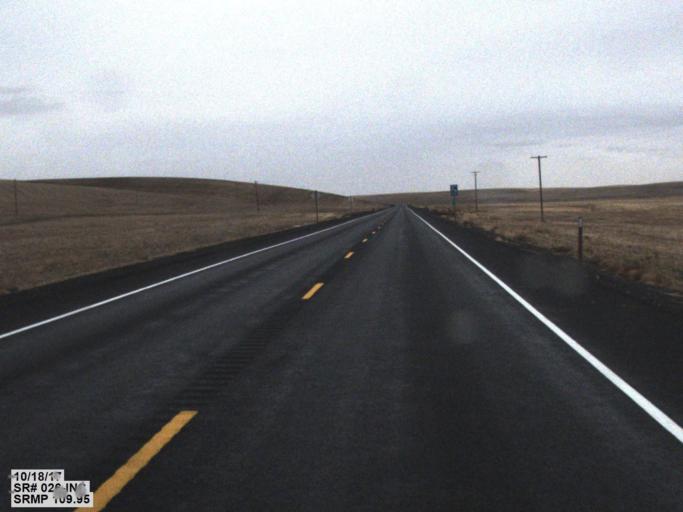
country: US
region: Washington
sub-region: Garfield County
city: Pomeroy
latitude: 46.8095
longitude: -117.7945
